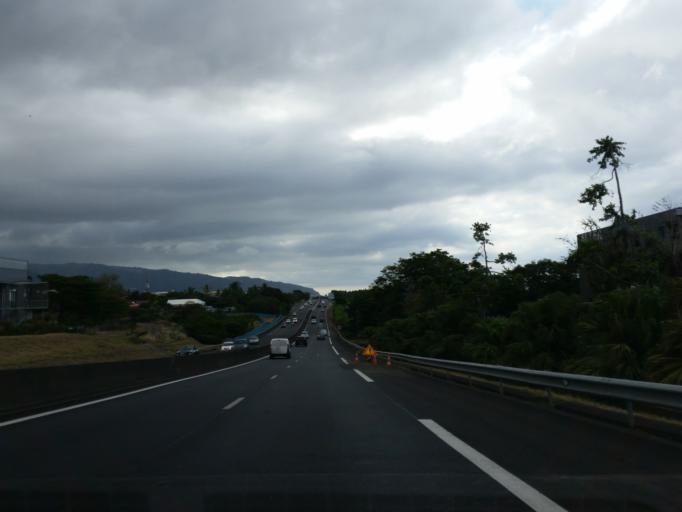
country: RE
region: Reunion
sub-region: Reunion
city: Sainte-Marie
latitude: -20.9005
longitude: 55.5279
